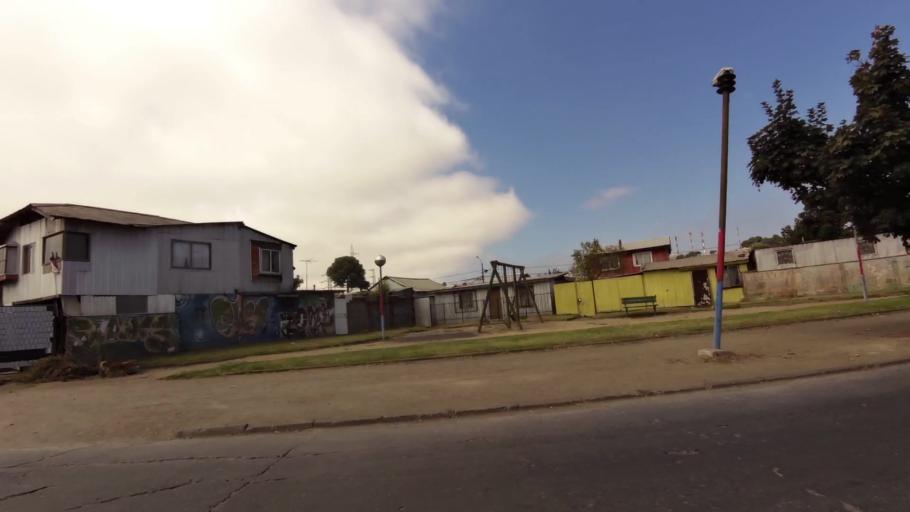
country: CL
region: Biobio
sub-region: Provincia de Concepcion
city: Concepcion
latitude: -36.8046
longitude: -73.0412
